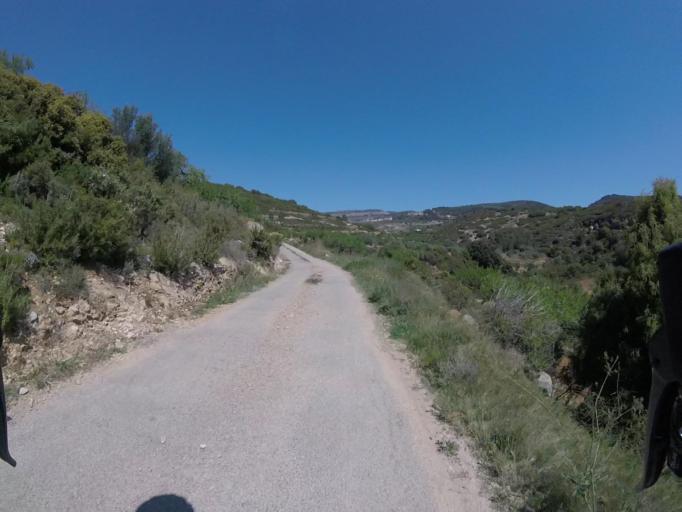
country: ES
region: Valencia
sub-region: Provincia de Castello
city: Sierra-Engarceran
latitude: 40.2537
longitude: -0.0253
